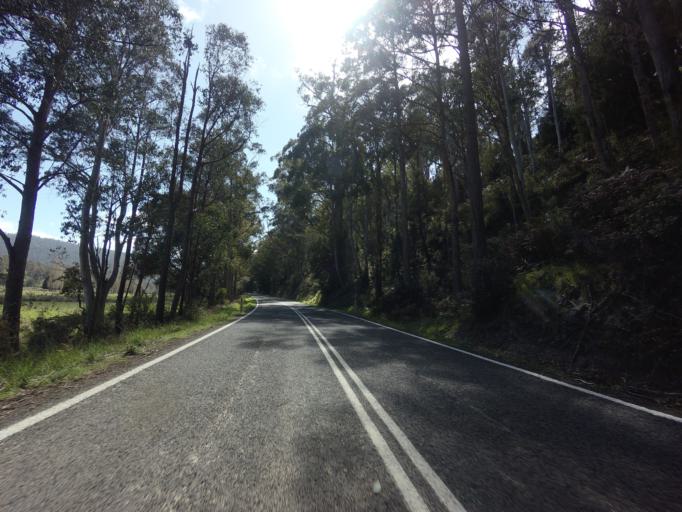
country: AU
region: Tasmania
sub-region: Derwent Valley
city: New Norfolk
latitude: -42.7022
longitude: 146.7139
